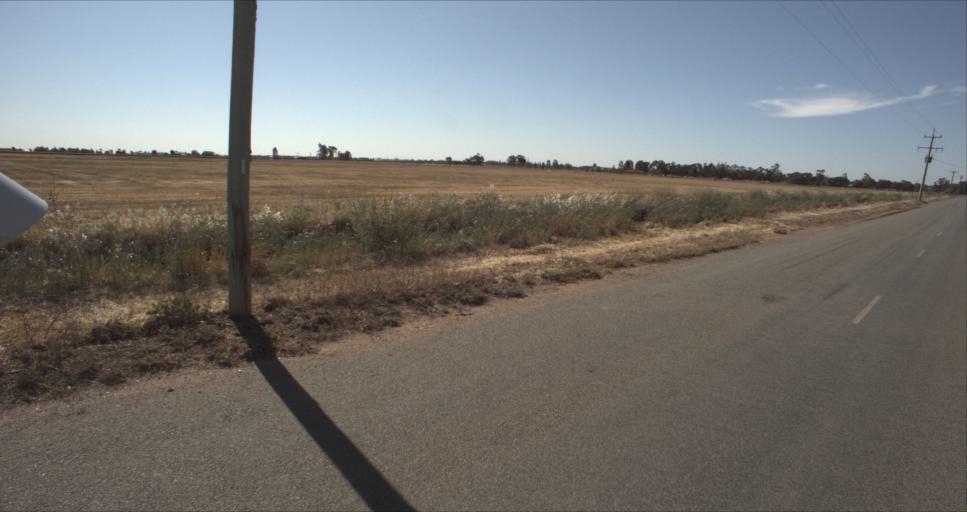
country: AU
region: New South Wales
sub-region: Leeton
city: Leeton
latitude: -34.5749
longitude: 146.3810
